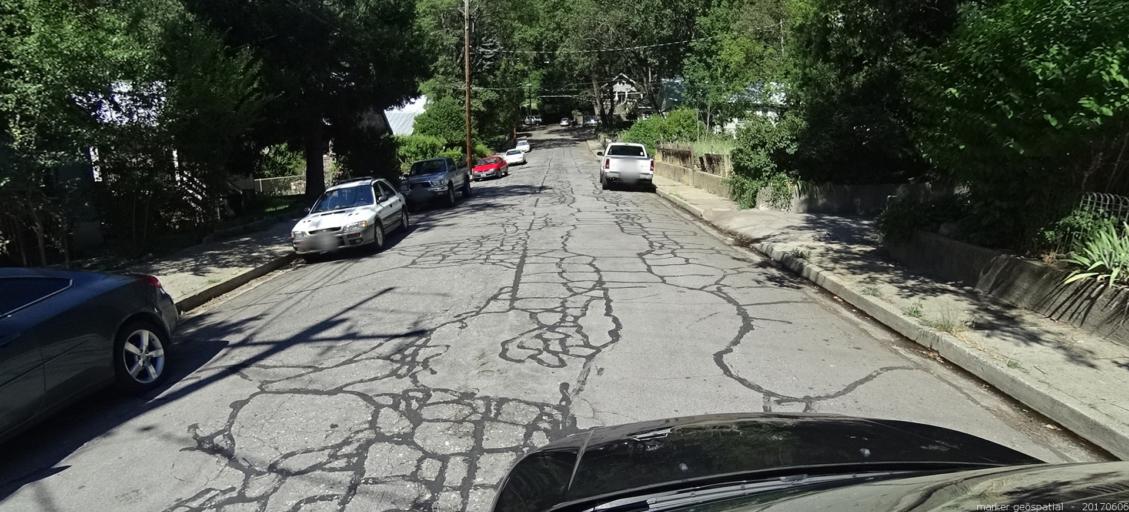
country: US
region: California
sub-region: Siskiyou County
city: Dunsmuir
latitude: 41.2062
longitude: -122.2747
